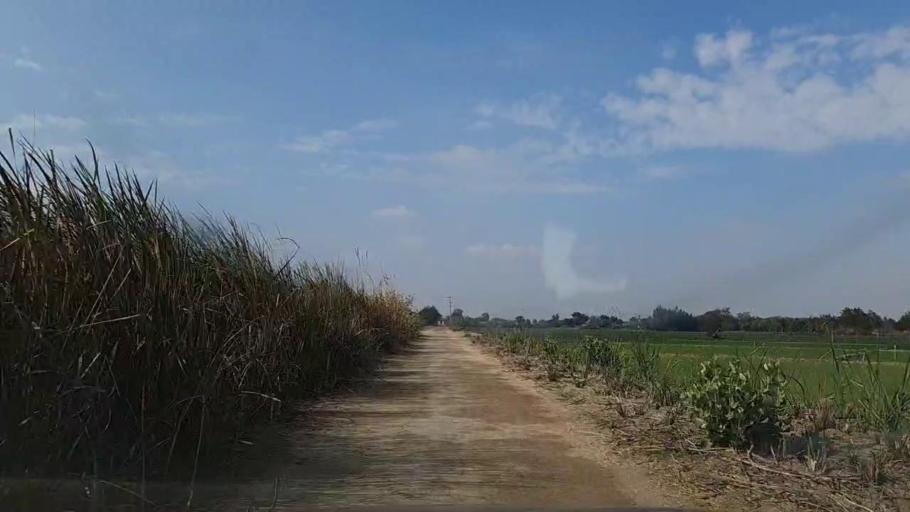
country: PK
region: Sindh
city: Sanghar
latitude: 26.2730
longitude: 69.0115
